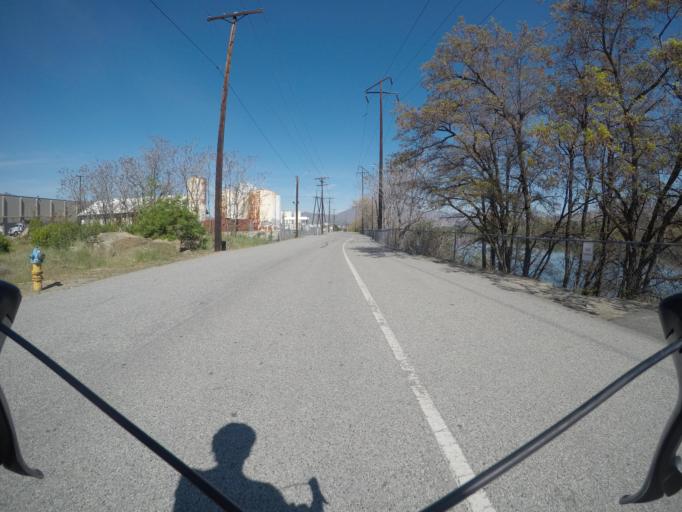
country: US
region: Washington
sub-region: Douglas County
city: East Wenatchee
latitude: 47.4165
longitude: -120.3015
